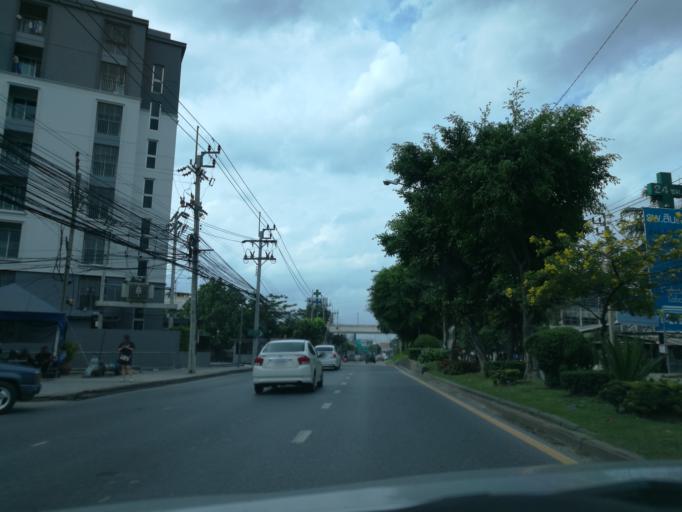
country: TH
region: Bangkok
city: Khan Na Yao
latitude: 13.8330
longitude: 100.6600
